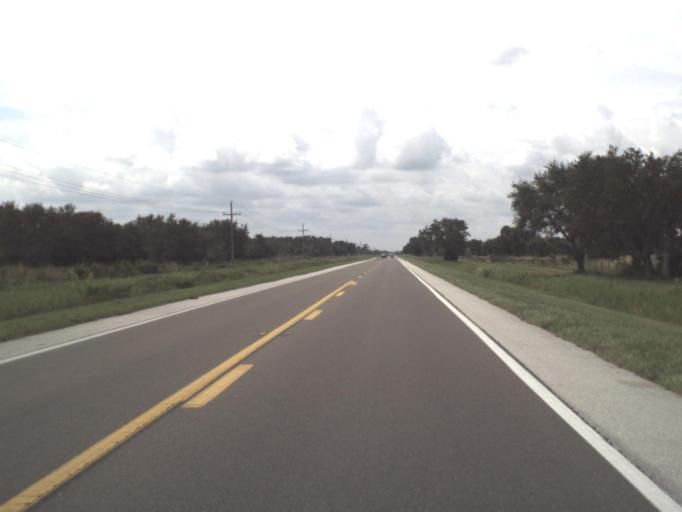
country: US
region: Florida
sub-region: Hendry County
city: LaBelle
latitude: 26.8103
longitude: -81.4147
